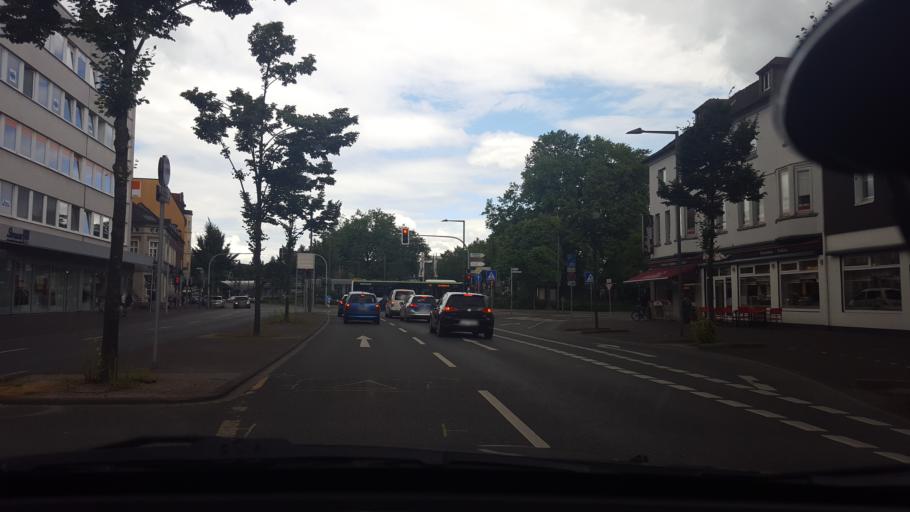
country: DE
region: North Rhine-Westphalia
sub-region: Regierungsbezirk Munster
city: Recklinghausen
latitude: 51.6141
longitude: 7.2019
